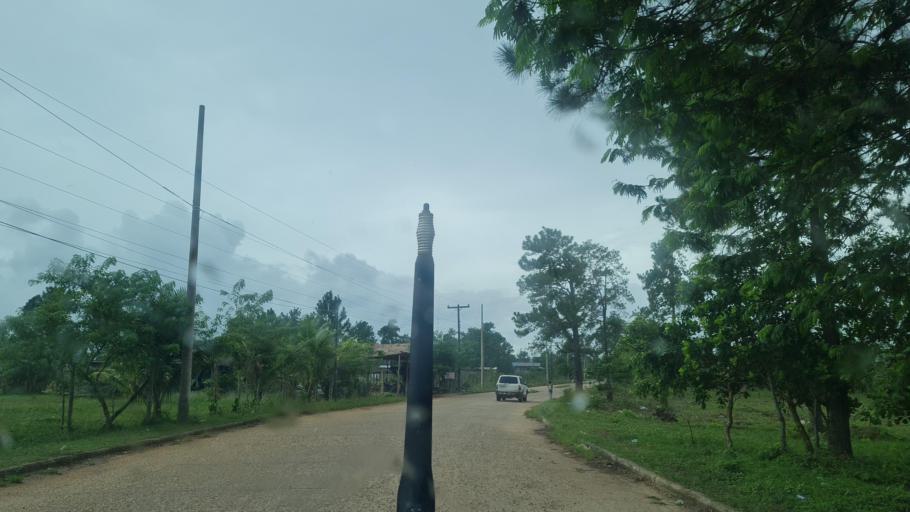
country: NI
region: Atlantico Norte (RAAN)
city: Waspam
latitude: 14.7241
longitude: -83.9737
